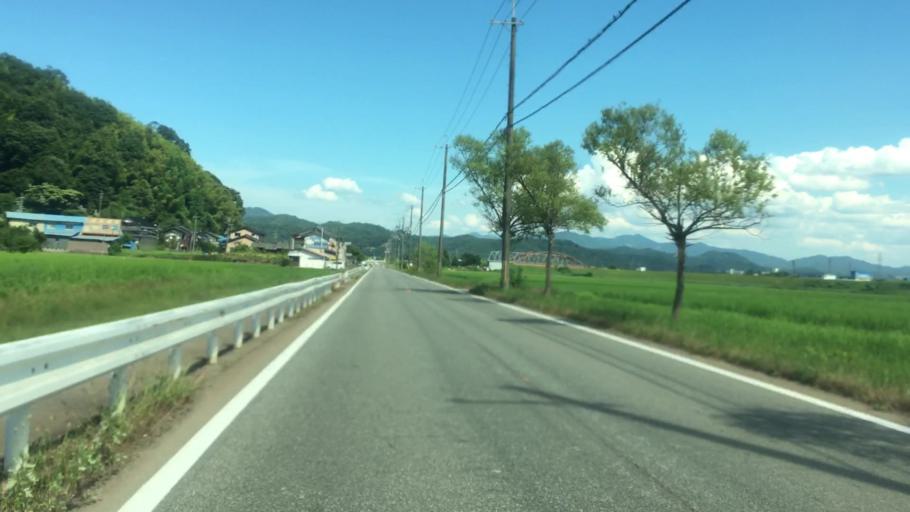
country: JP
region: Hyogo
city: Toyooka
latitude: 35.5666
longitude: 134.7965
